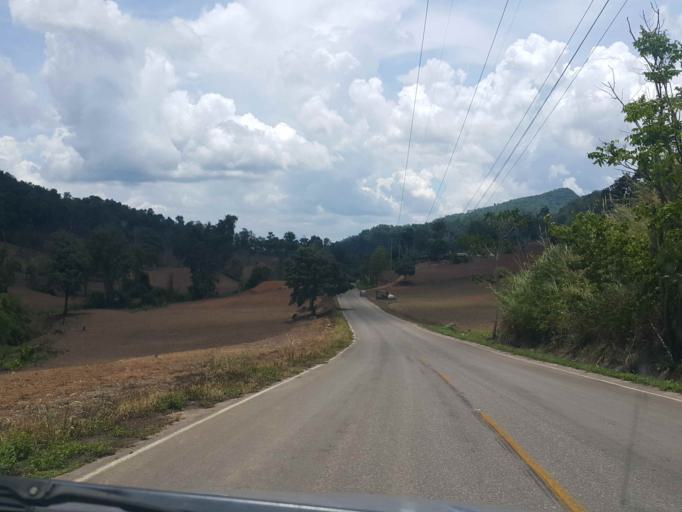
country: TH
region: Phayao
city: Chiang Muan
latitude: 18.9072
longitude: 100.1190
